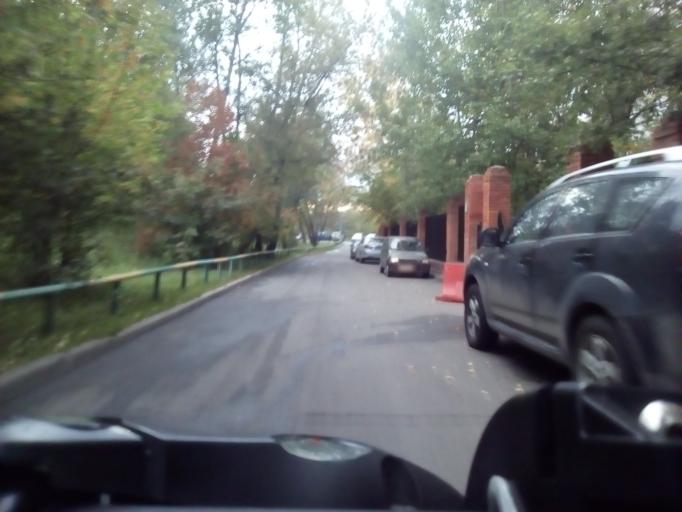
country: RU
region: Moscow
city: Sviblovo
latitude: 55.8530
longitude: 37.6378
